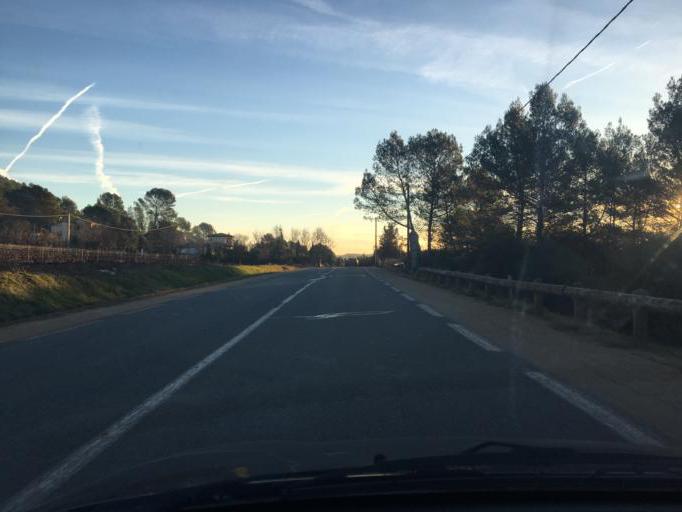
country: FR
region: Provence-Alpes-Cote d'Azur
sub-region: Departement du Var
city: Taradeau
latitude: 43.4490
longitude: 6.4362
